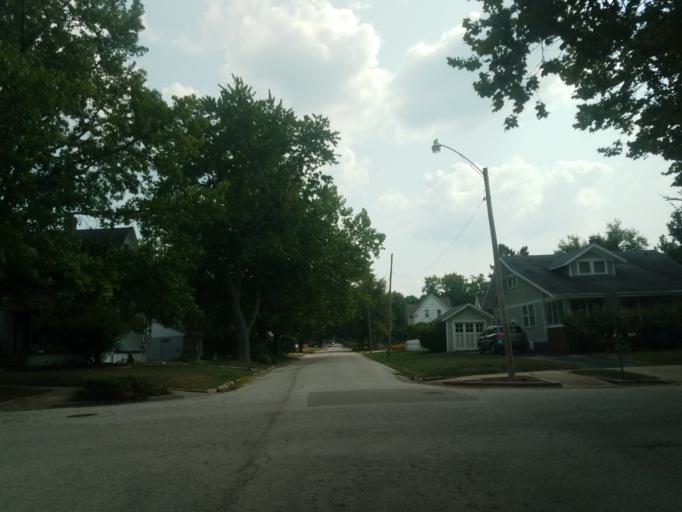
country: US
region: Illinois
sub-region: McLean County
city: Bloomington
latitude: 40.4775
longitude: -88.9652
